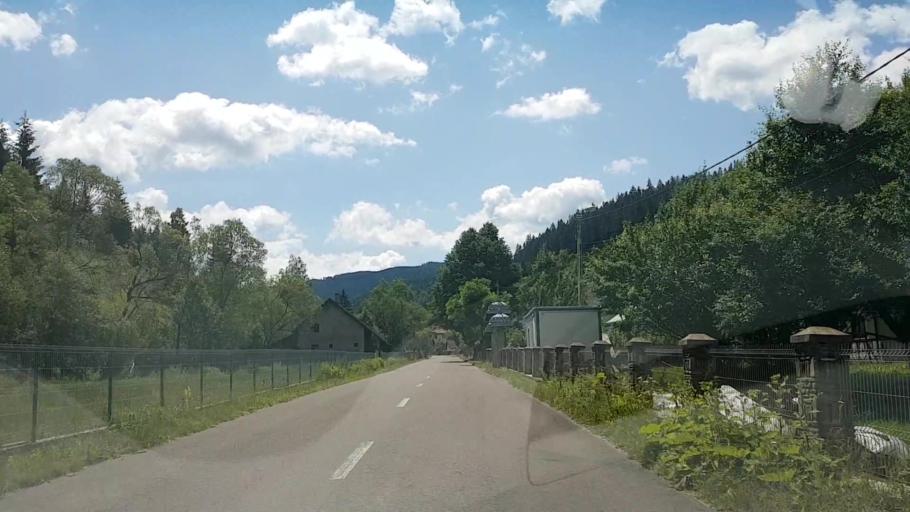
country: RO
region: Suceava
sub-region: Comuna Pojorata
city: Pojorata
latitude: 47.4917
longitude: 25.4855
